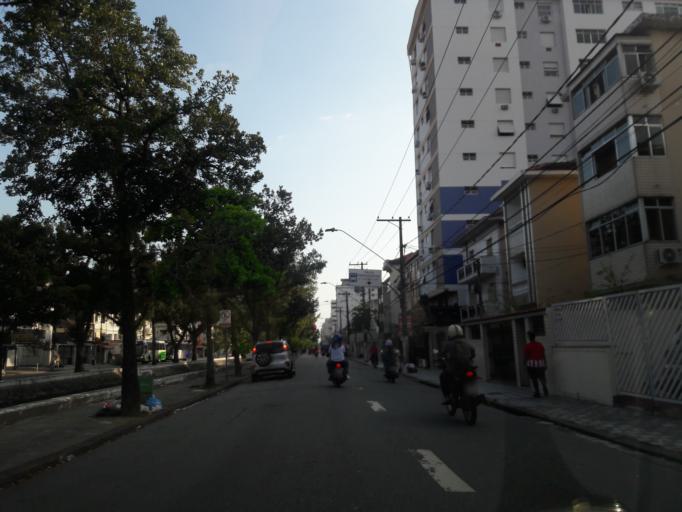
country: BR
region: Sao Paulo
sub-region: Santos
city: Santos
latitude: -23.9559
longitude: -46.3378
